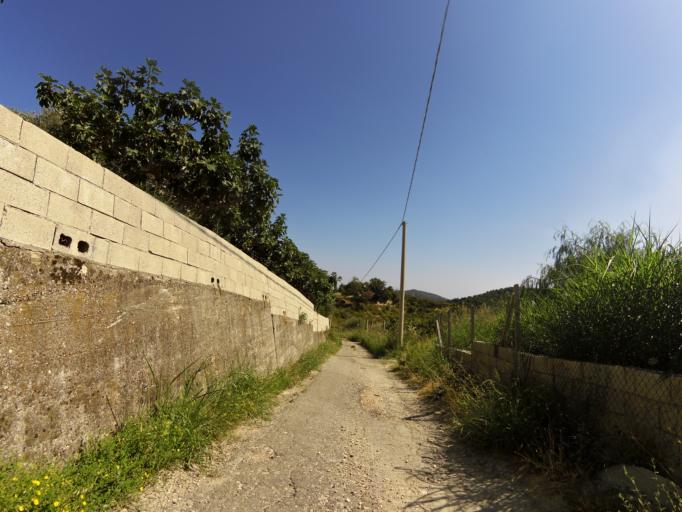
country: IT
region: Calabria
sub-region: Provincia di Reggio Calabria
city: Pazzano
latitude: 38.4606
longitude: 16.4550
